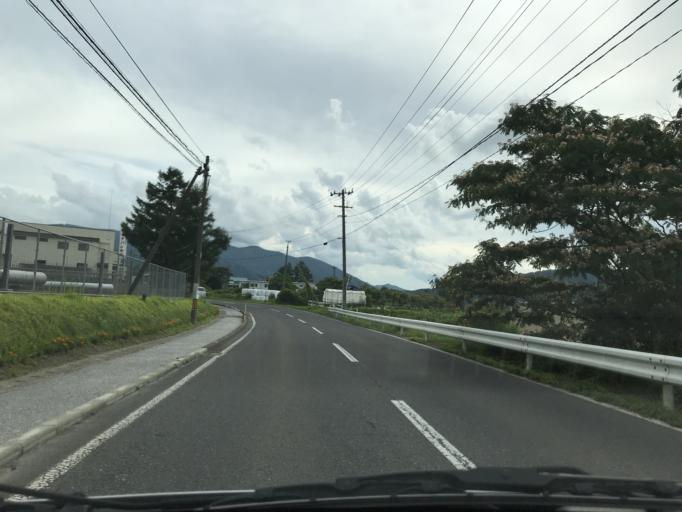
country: JP
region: Iwate
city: Tono
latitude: 39.3484
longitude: 141.5470
